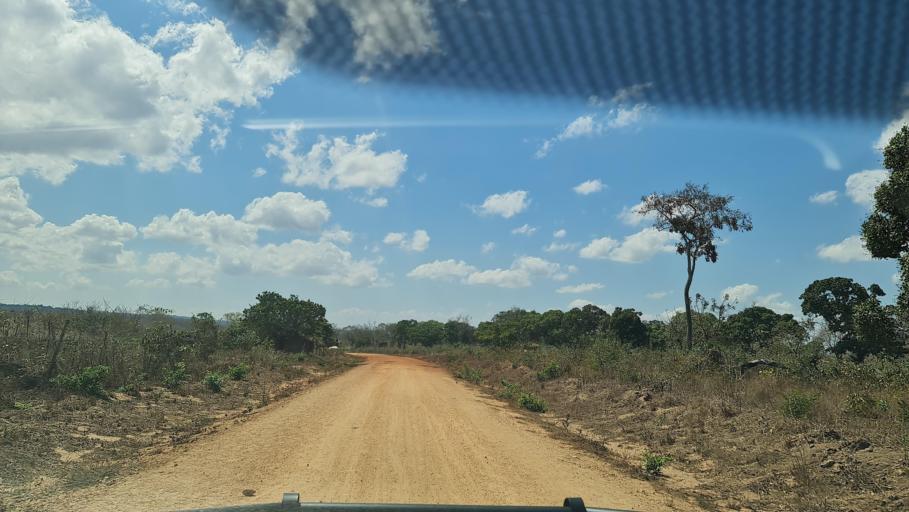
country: MZ
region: Nampula
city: Nacala
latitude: -14.1794
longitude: 40.2214
